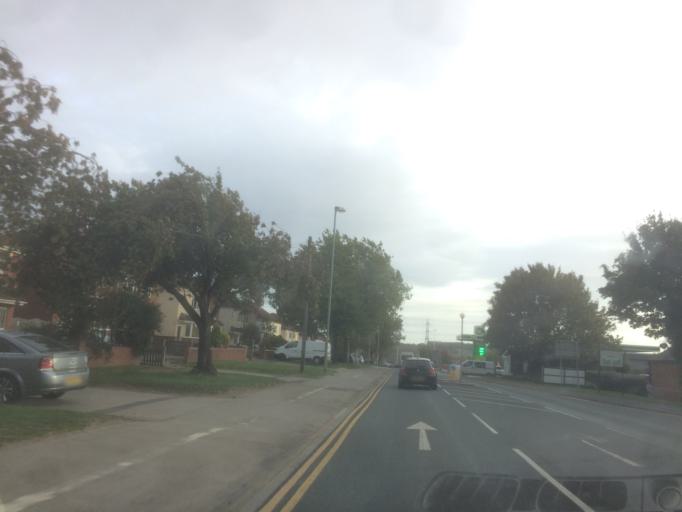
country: GB
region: England
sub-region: City and Borough of Wakefield
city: Pontefract
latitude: 53.7131
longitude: -1.3340
